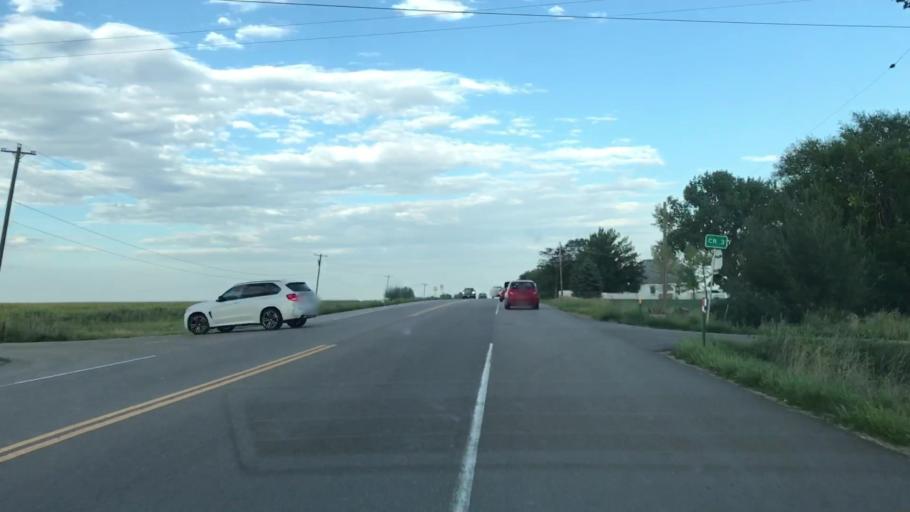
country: US
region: Colorado
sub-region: Weld County
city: Mead
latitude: 40.2038
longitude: -105.0366
